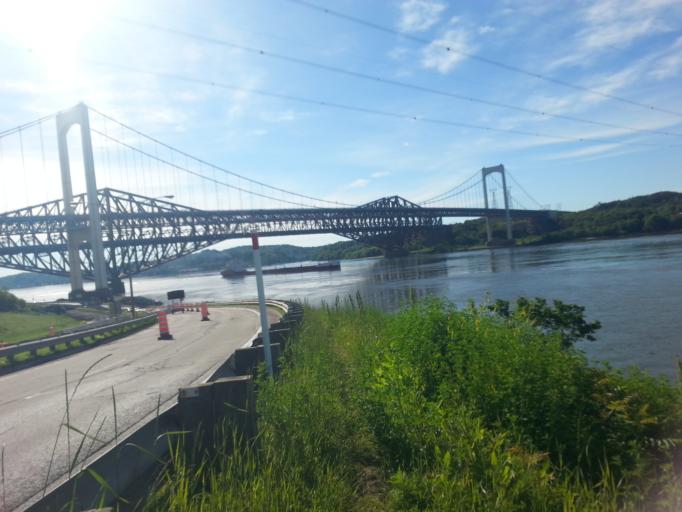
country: CA
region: Quebec
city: L'Ancienne-Lorette
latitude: 46.7485
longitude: -71.2975
